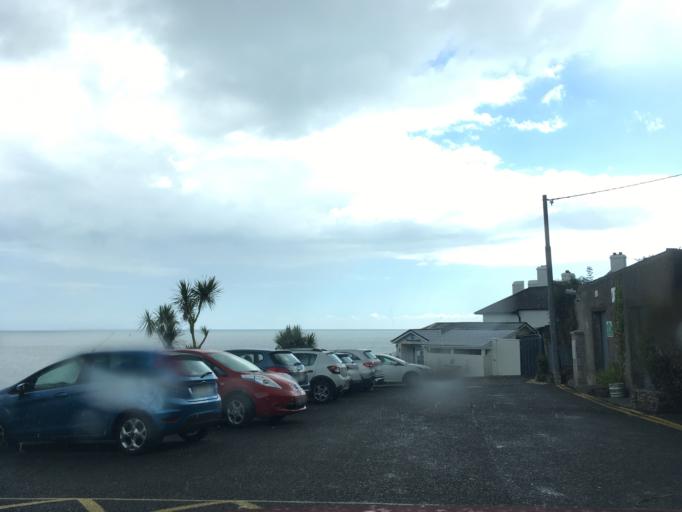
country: IE
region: Munster
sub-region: County Cork
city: Crosshaven
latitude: 51.7811
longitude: -8.2943
